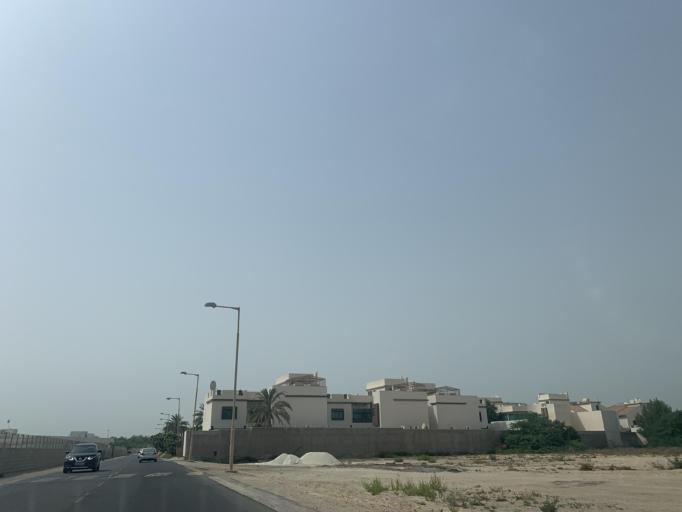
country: BH
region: Manama
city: Jidd Hafs
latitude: 26.1986
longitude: 50.4727
